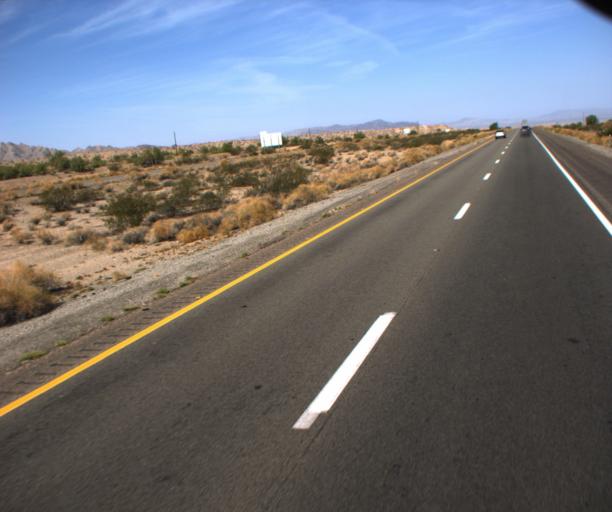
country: US
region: Arizona
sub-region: Mohave County
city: Desert Hills
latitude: 34.7292
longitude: -114.3353
